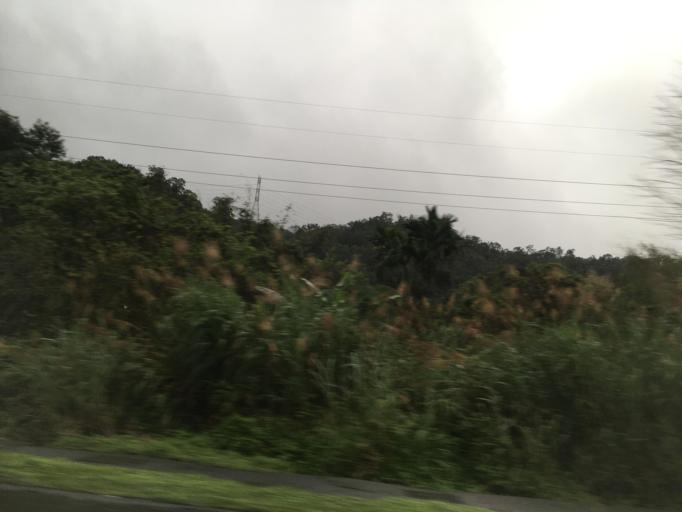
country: TW
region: Taiwan
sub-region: Keelung
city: Keelung
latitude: 25.0252
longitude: 121.8220
